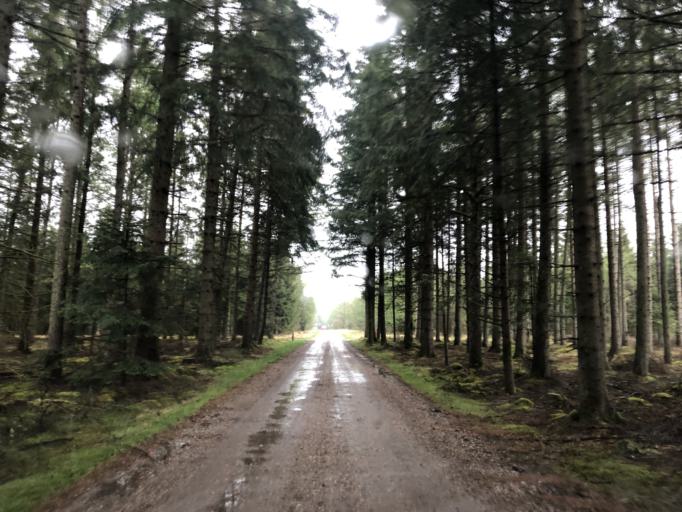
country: DK
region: Central Jutland
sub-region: Lemvig Kommune
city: Lemvig
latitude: 56.4596
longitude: 8.3978
